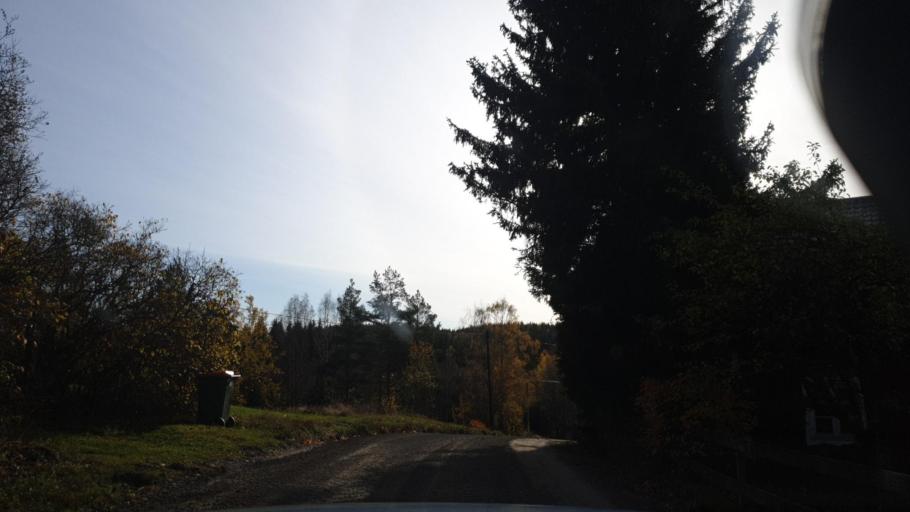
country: NO
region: Hedmark
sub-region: Eidskog
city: Skotterud
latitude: 59.7329
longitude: 12.0965
